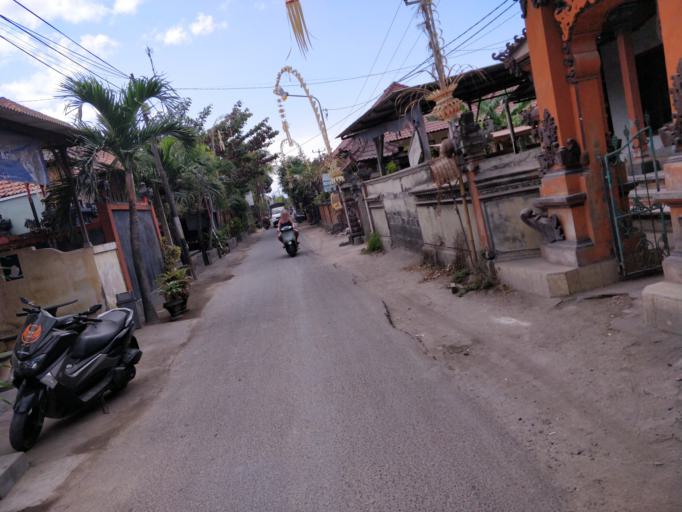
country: ID
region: Bali
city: Jungutbatu Kaja Dua
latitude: -8.6730
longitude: 115.4493
